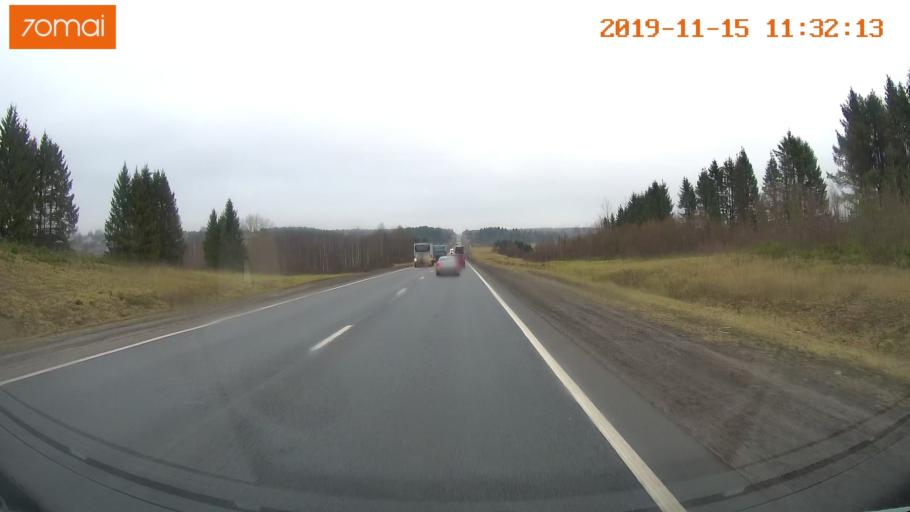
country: RU
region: Vologda
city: Molochnoye
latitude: 59.1847
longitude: 39.5696
